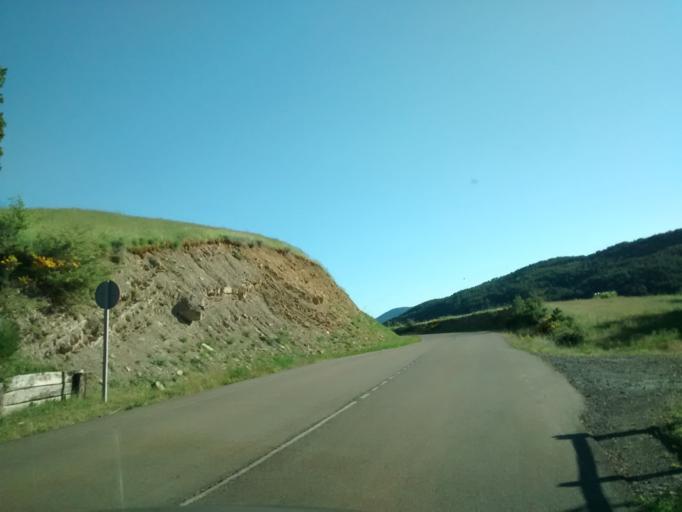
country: ES
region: Aragon
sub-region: Provincia de Huesca
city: Borau
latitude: 42.6761
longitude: -0.6201
